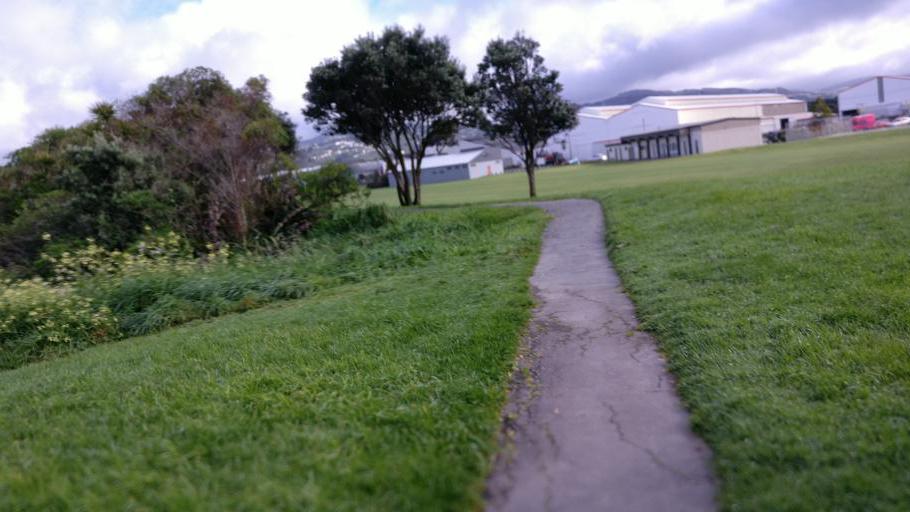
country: NZ
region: Wellington
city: Petone
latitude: -41.2360
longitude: 174.8960
